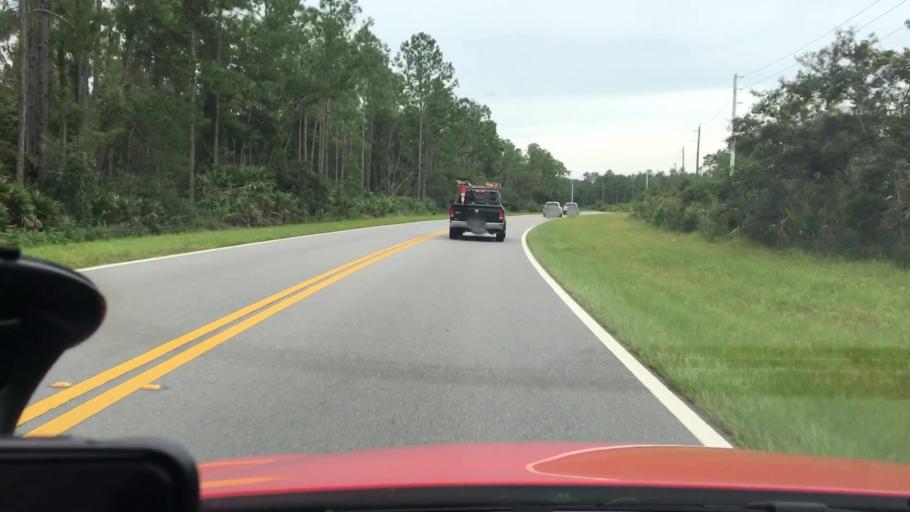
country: US
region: Florida
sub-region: Flagler County
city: Palm Coast
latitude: 29.5317
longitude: -81.2020
